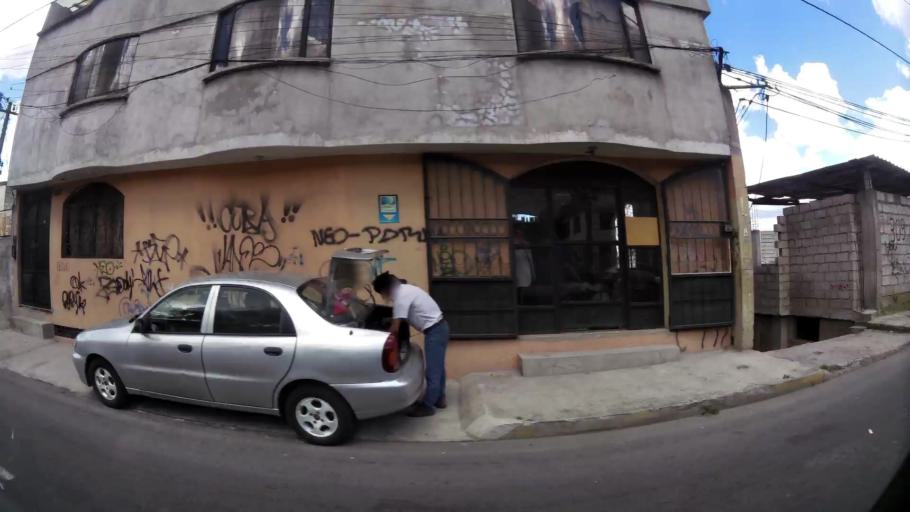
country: EC
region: Pichincha
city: Quito
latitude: -0.1902
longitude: -78.5123
